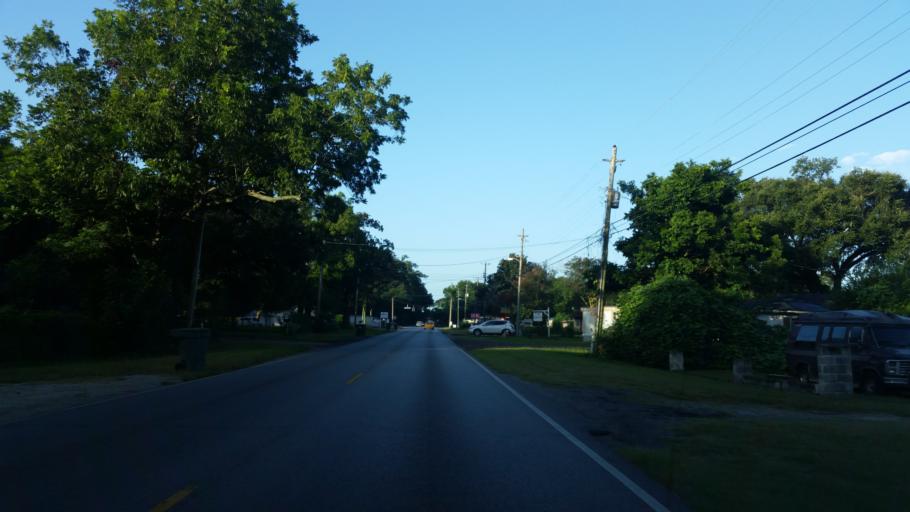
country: US
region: Florida
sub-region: Escambia County
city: West Pensacola
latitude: 30.4203
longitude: -87.2717
